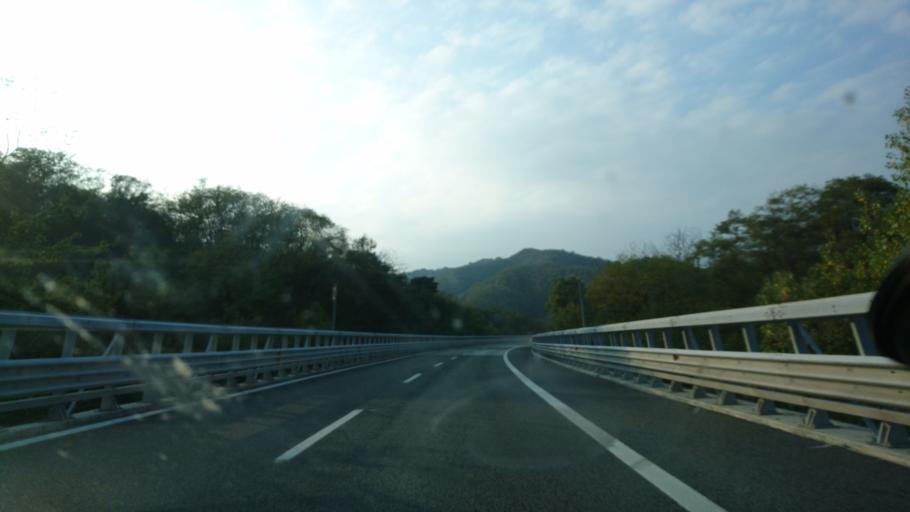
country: IT
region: Liguria
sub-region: Provincia di Savona
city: Altare
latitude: 44.3247
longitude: 8.3718
